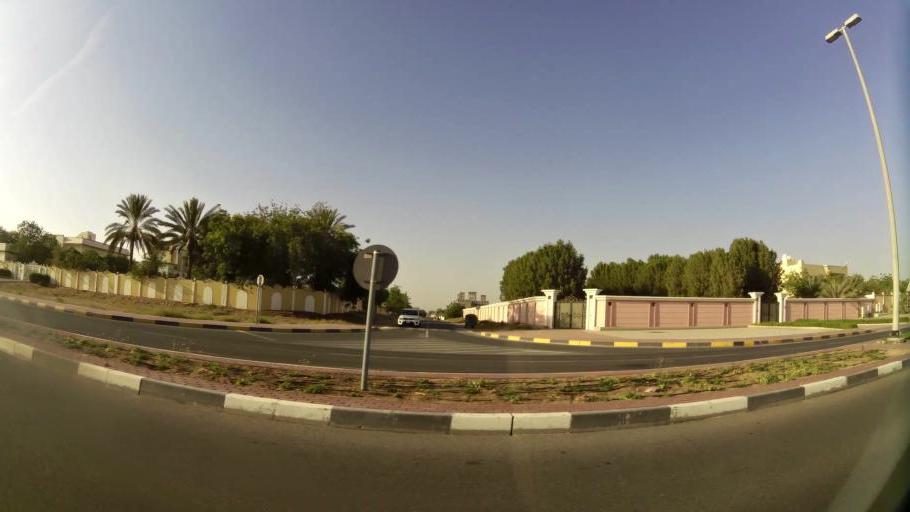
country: AE
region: Ajman
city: Ajman
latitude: 25.4060
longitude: 55.4922
